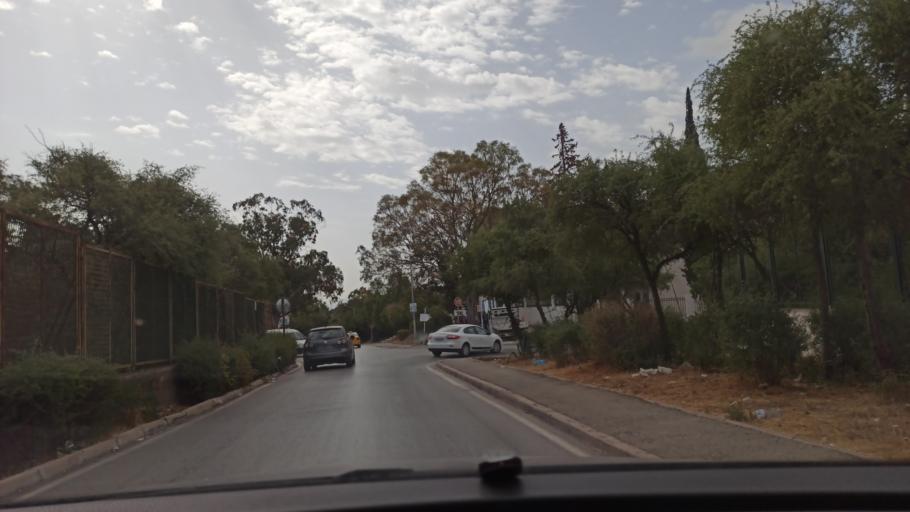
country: TN
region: Tunis
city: Tunis
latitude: 36.8192
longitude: 10.1696
